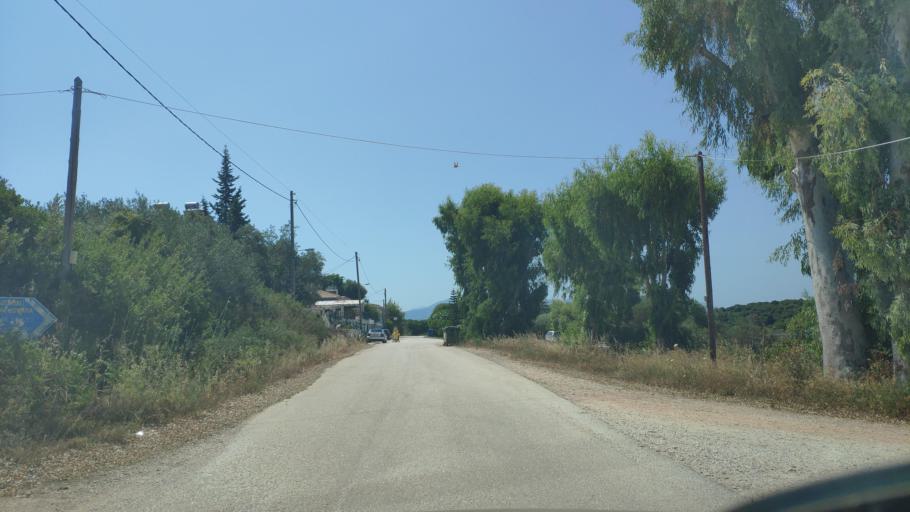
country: GR
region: Epirus
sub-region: Nomos Artas
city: Aneza
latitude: 39.0128
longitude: 20.9183
